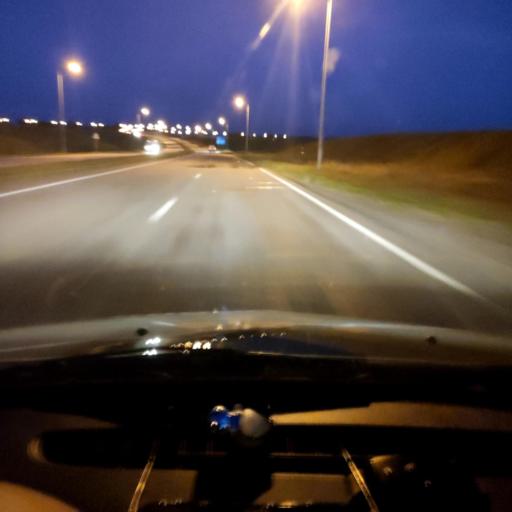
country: RU
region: Belgorod
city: Skorodnoye
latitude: 51.0642
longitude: 37.2031
